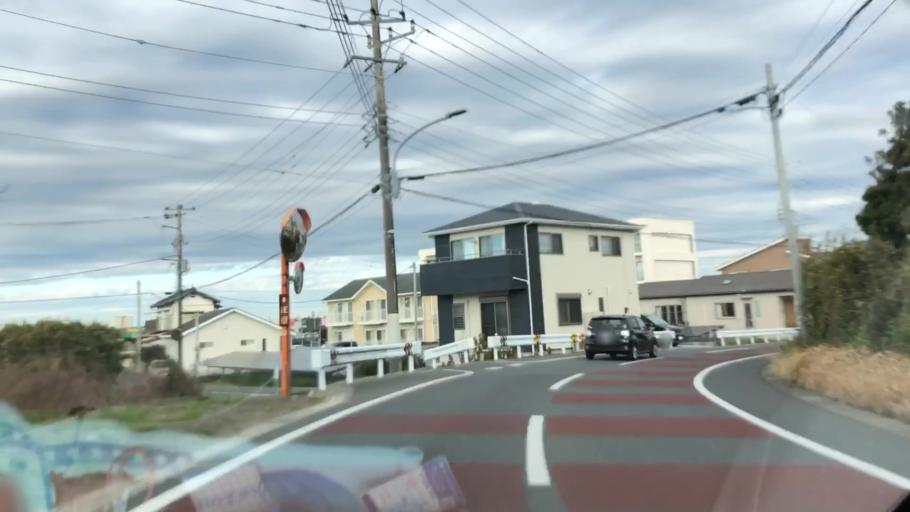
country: JP
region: Chiba
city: Tateyama
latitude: 35.0064
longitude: 139.8756
